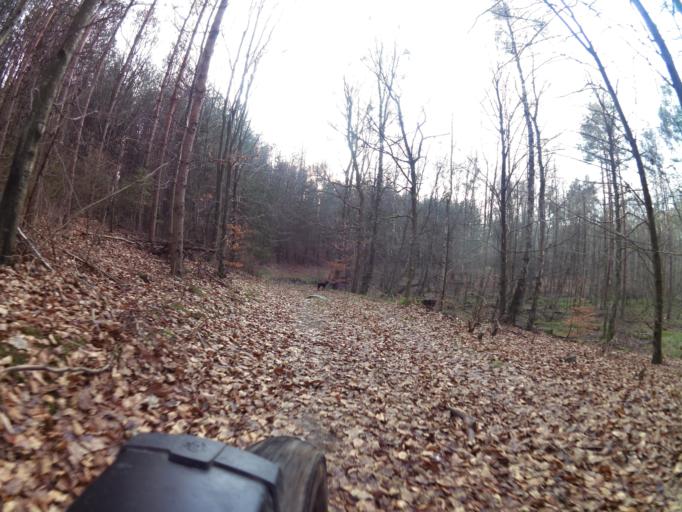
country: PL
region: West Pomeranian Voivodeship
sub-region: Powiat koszalinski
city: Polanow
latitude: 54.1885
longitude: 16.7290
